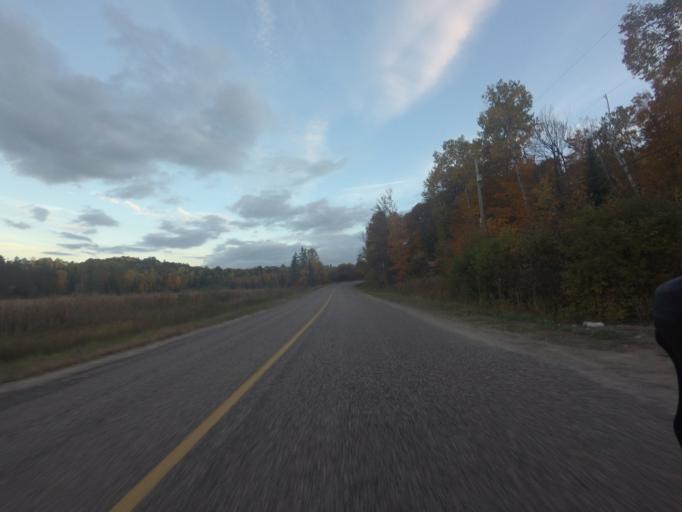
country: CA
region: Ontario
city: Renfrew
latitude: 45.3998
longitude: -76.9506
